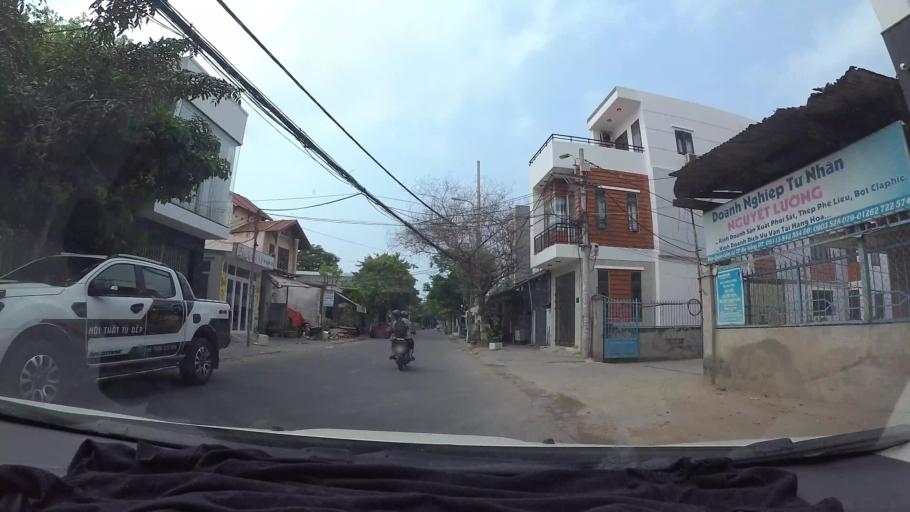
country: VN
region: Da Nang
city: Thanh Khe
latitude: 16.0544
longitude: 108.1790
